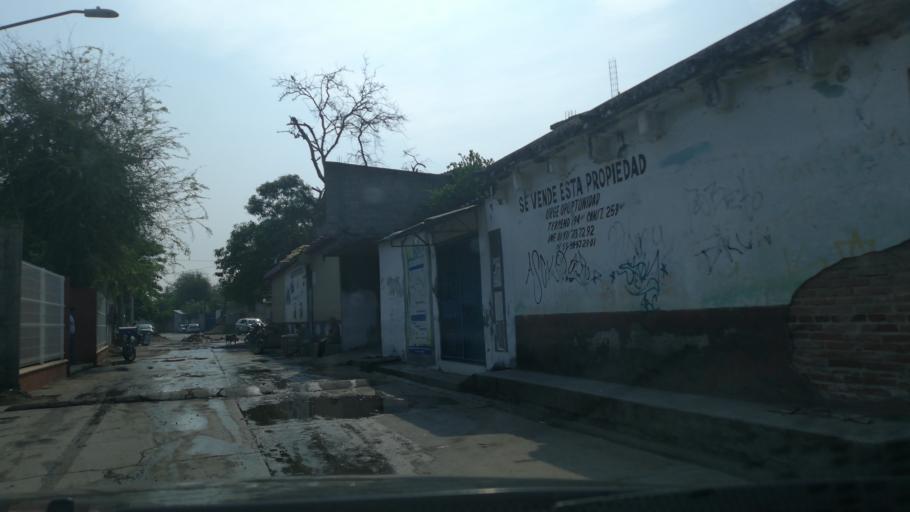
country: MX
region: Oaxaca
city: San Blas Atempa
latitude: 16.3371
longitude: -95.2272
